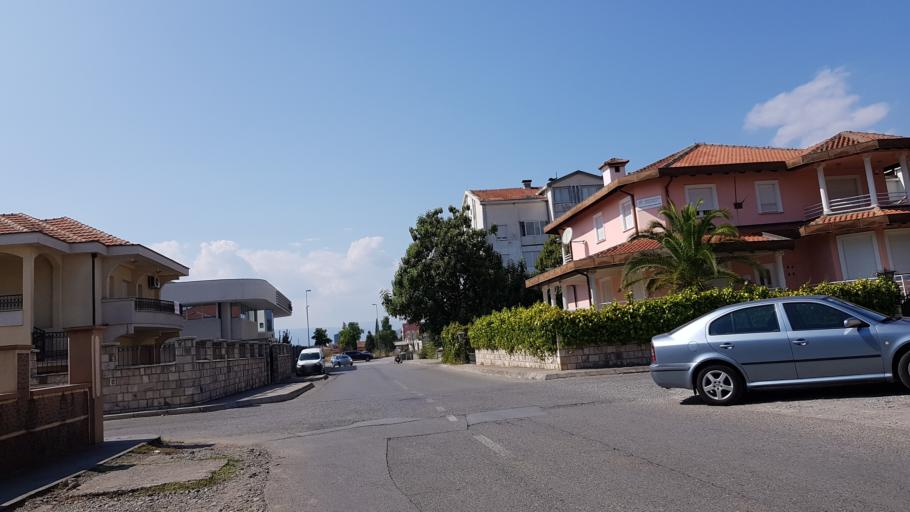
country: ME
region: Podgorica
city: Podgorica
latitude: 42.4336
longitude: 19.2755
